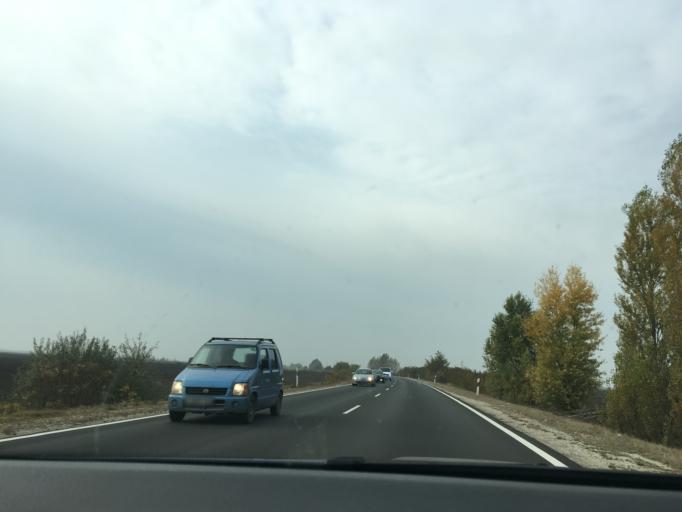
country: HU
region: Pest
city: Abony
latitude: 47.2105
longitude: 20.0649
